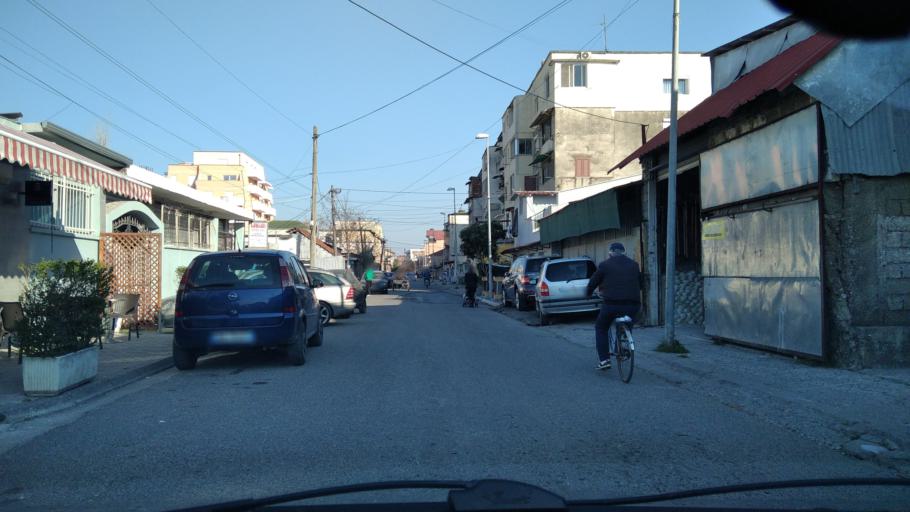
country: AL
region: Shkoder
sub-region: Rrethi i Shkodres
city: Shkoder
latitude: 42.0583
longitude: 19.5150
